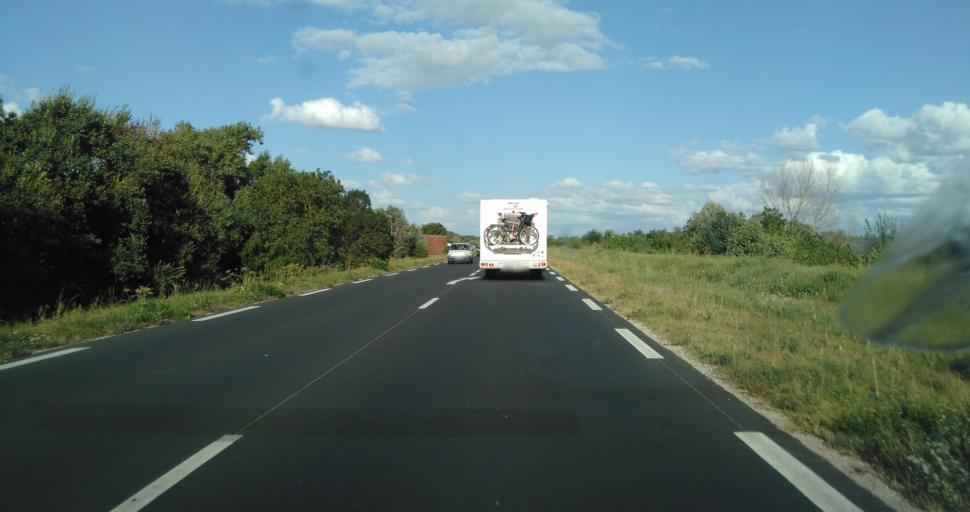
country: FR
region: Centre
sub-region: Departement d'Indre-et-Loire
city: Nazelles-Negron
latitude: 47.4054
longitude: 0.9330
